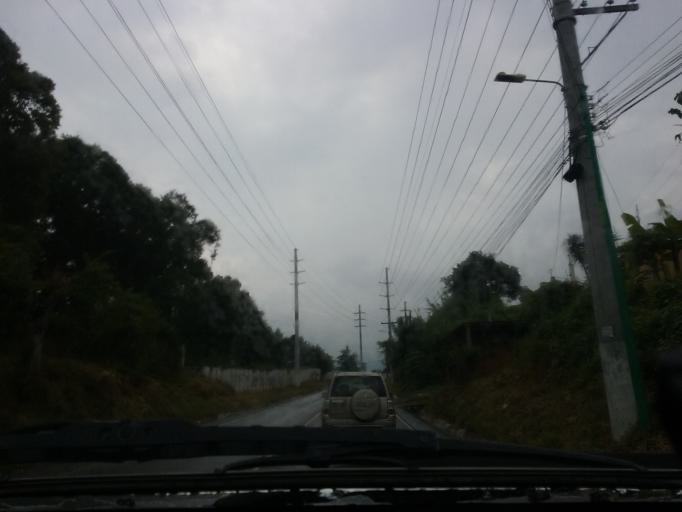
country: GT
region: Guatemala
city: Villa Nueva
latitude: 14.5421
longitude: -90.6030
